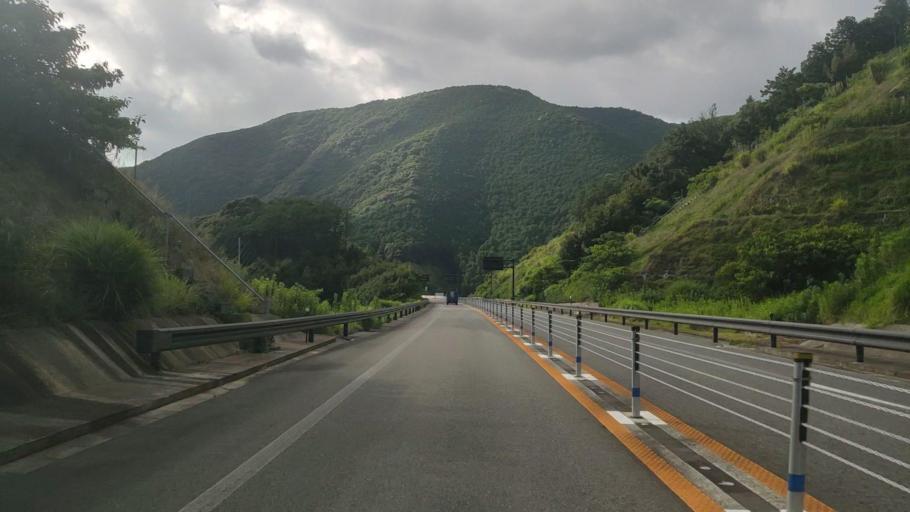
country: JP
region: Wakayama
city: Tanabe
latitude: 33.5588
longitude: 135.5070
